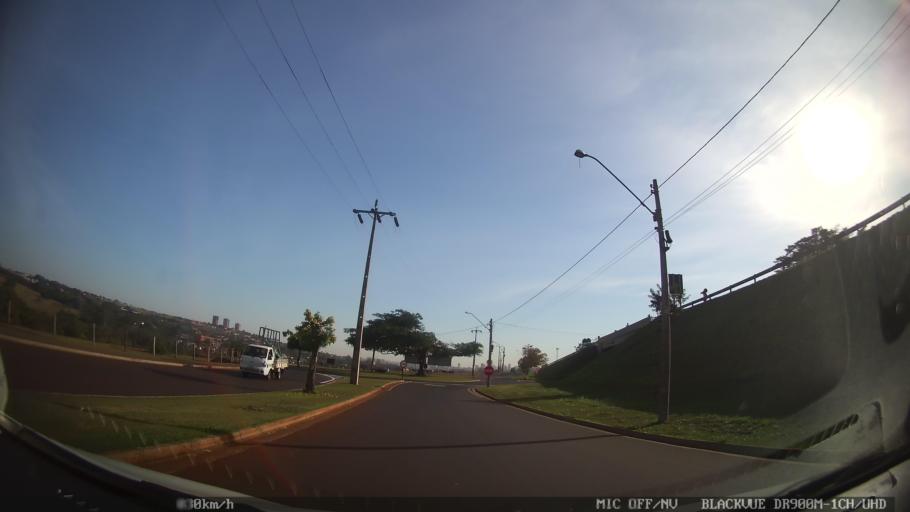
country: BR
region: Sao Paulo
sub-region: Ribeirao Preto
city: Ribeirao Preto
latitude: -21.2561
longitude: -47.8193
